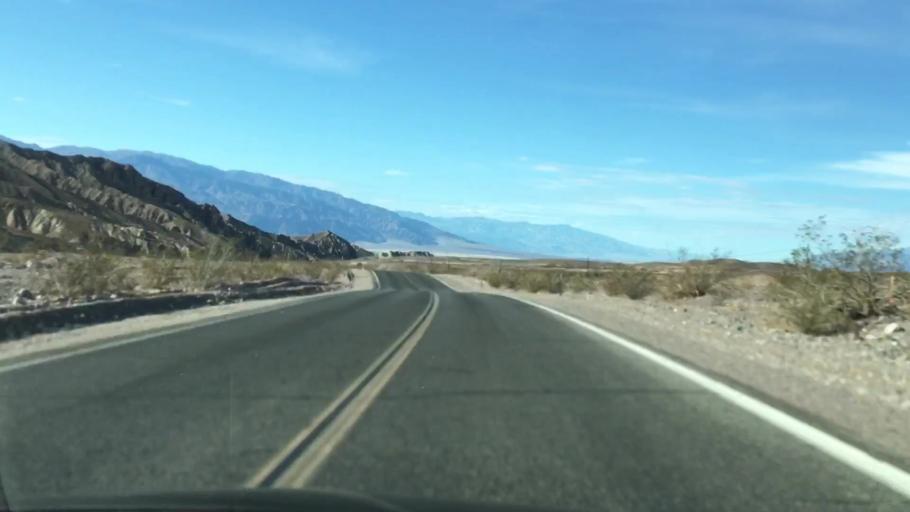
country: US
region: Nevada
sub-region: Nye County
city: Beatty
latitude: 36.4357
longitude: -116.8195
